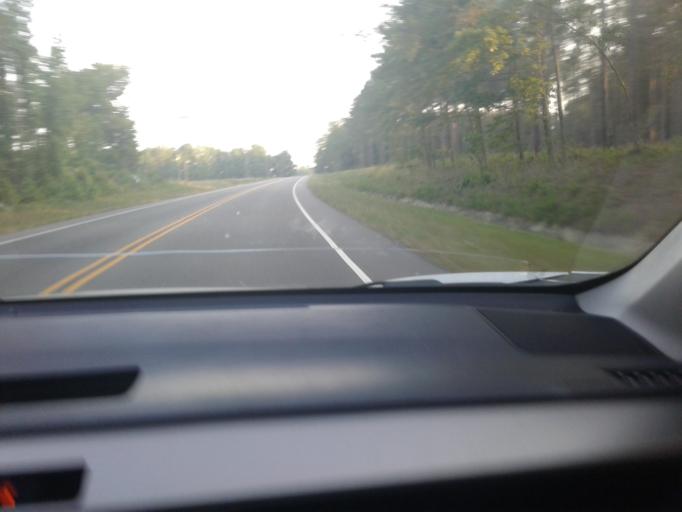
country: US
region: North Carolina
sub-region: Harnett County
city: Lillington
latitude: 35.4301
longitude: -78.8260
